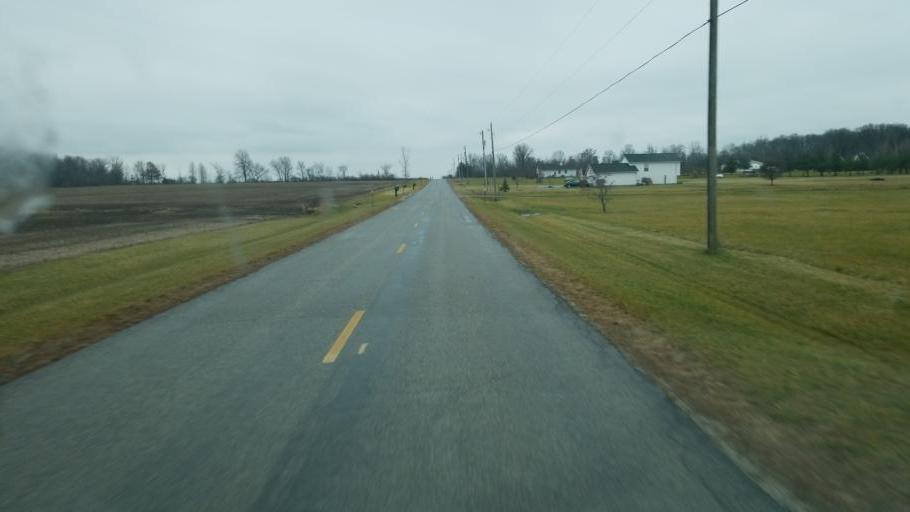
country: US
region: Ohio
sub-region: Delaware County
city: Delaware
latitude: 40.3509
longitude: -83.0212
